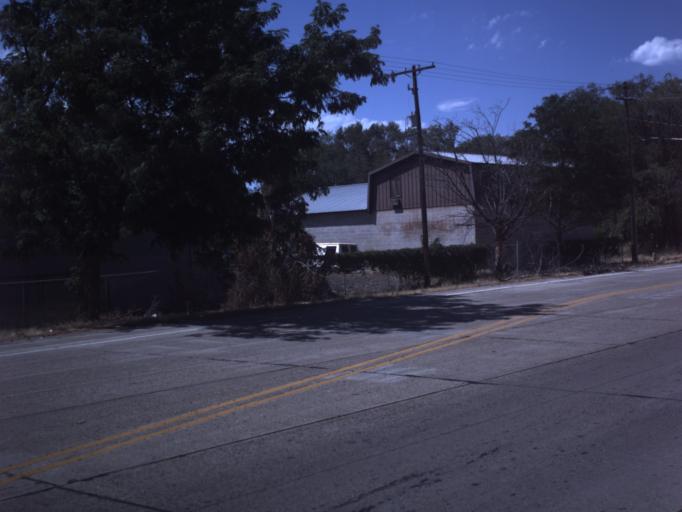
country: US
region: Utah
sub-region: Weber County
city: Ogden
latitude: 41.2311
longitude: -111.9811
